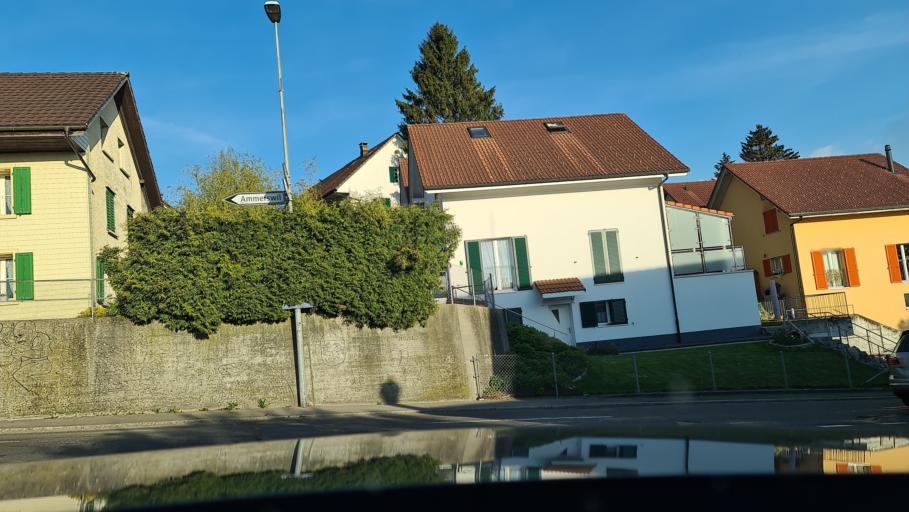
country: CH
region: Aargau
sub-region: Bezirk Lenzburg
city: Egliswil
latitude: 47.3491
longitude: 8.1876
